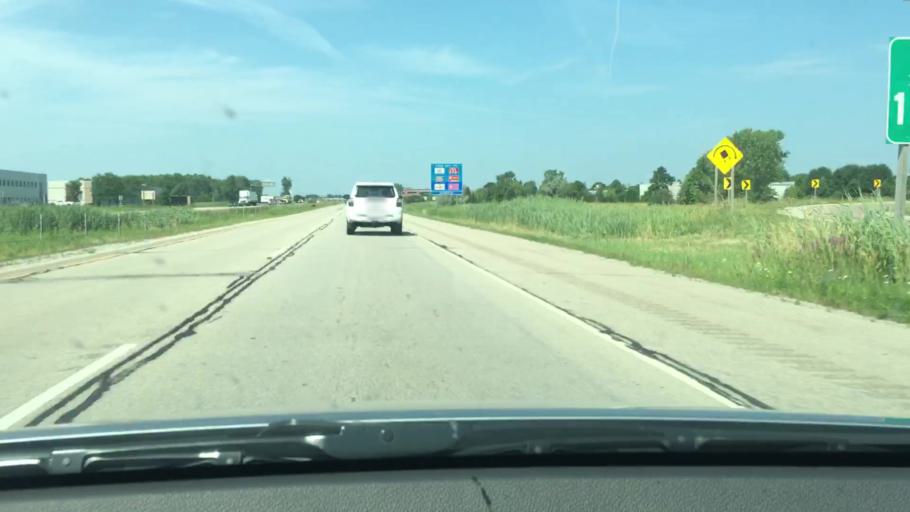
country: US
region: Wisconsin
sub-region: Outagamie County
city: Kimberly
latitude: 44.2982
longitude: -88.3573
